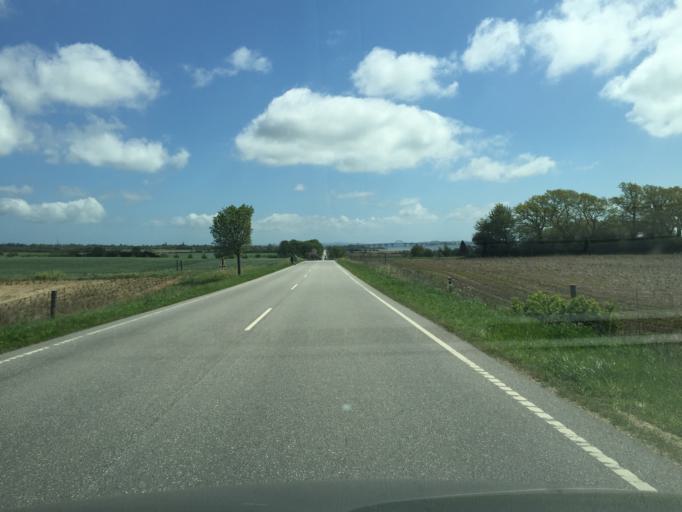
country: DK
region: Zealand
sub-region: Guldborgsund Kommune
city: Stubbekobing
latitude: 54.9983
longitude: 12.0990
